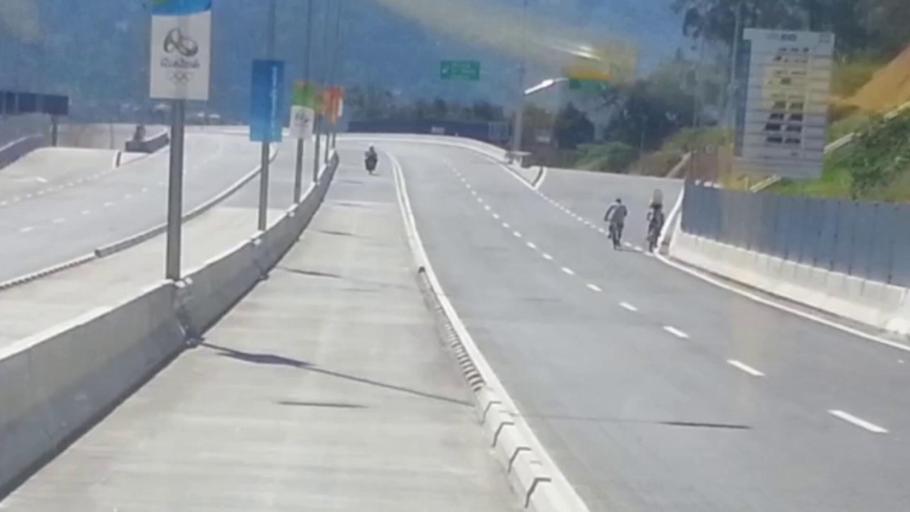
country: BR
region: Rio de Janeiro
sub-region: Nilopolis
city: Nilopolis
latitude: -22.9222
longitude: -43.3974
